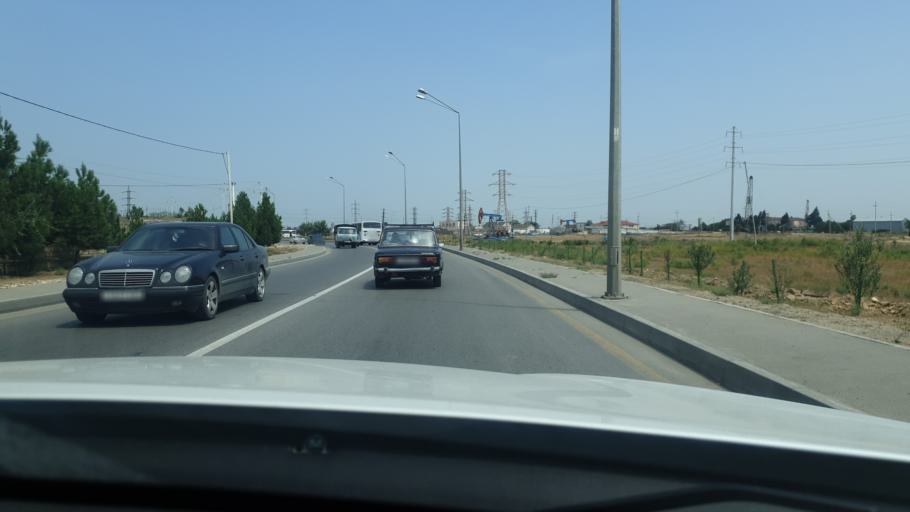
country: AZ
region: Baki
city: Qaracuxur
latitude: 40.3936
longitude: 49.9921
